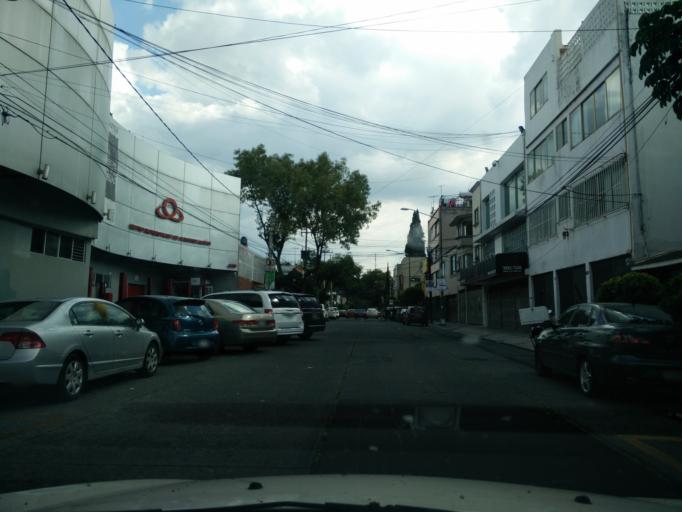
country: MX
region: Mexico City
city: Colonia del Valle
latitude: 19.3768
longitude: -99.1566
